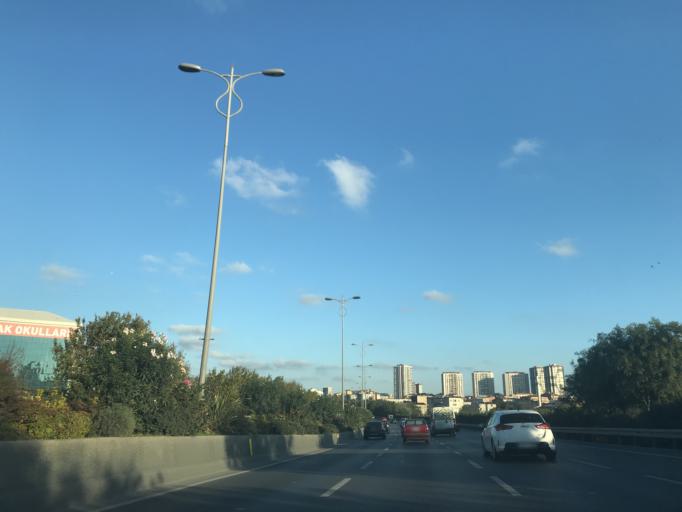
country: TR
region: Istanbul
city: Bagcilar
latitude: 41.0574
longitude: 28.8470
